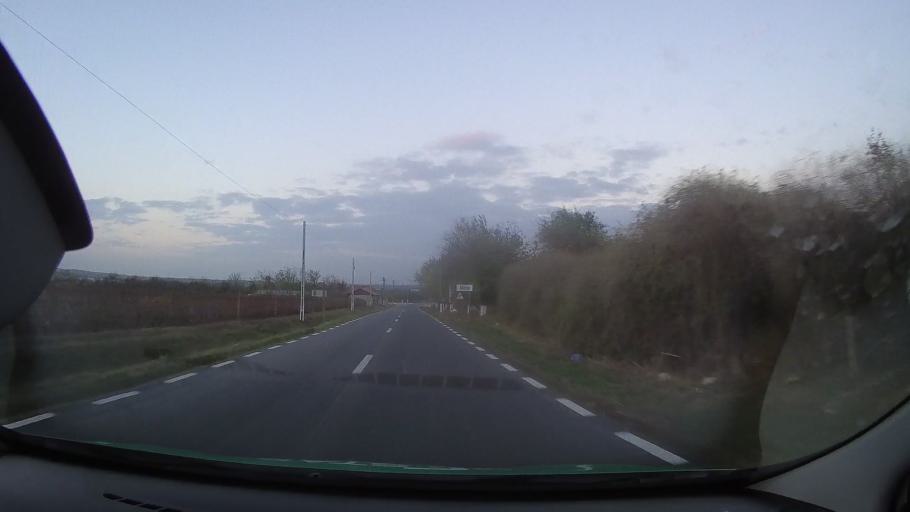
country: RO
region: Constanta
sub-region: Comuna Oltina
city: Oltina
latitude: 44.1555
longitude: 27.6675
